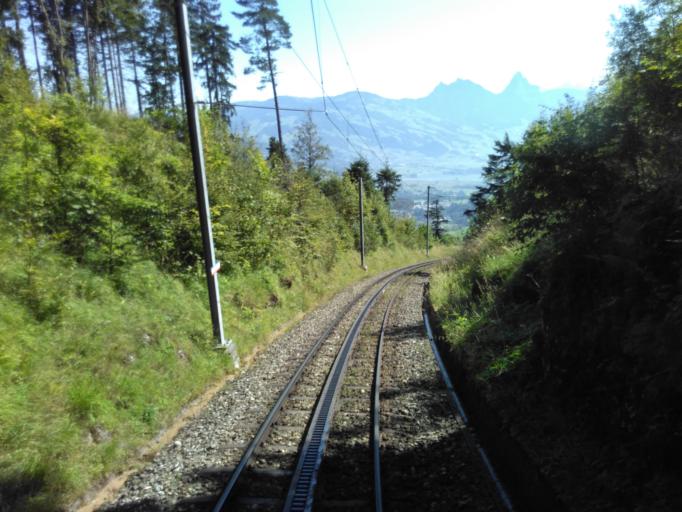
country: CH
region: Schwyz
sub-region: Bezirk Schwyz
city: Arth
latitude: 47.0407
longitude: 8.5185
